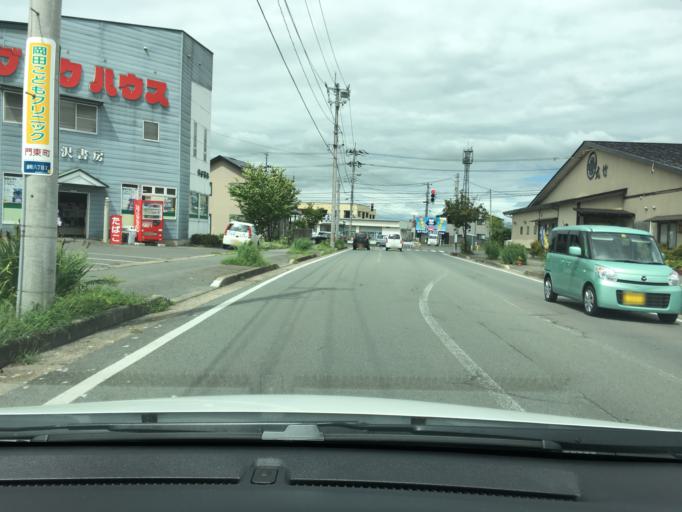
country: JP
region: Yamagata
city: Yonezawa
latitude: 37.8996
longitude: 140.1237
